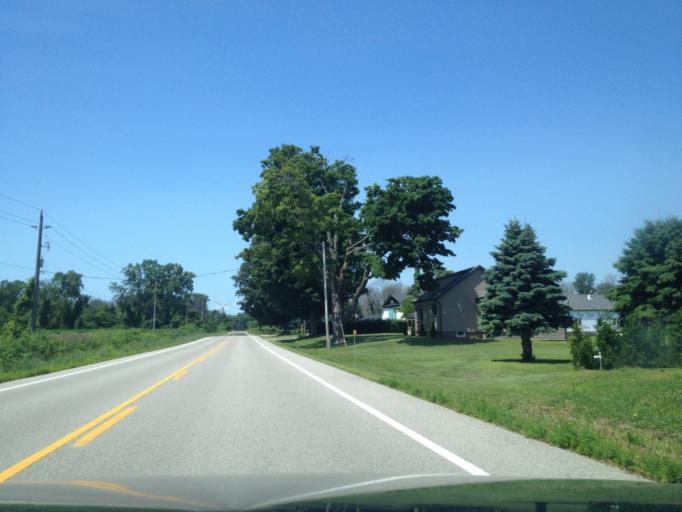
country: CA
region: Ontario
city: Norfolk County
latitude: 42.5840
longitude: -80.6068
